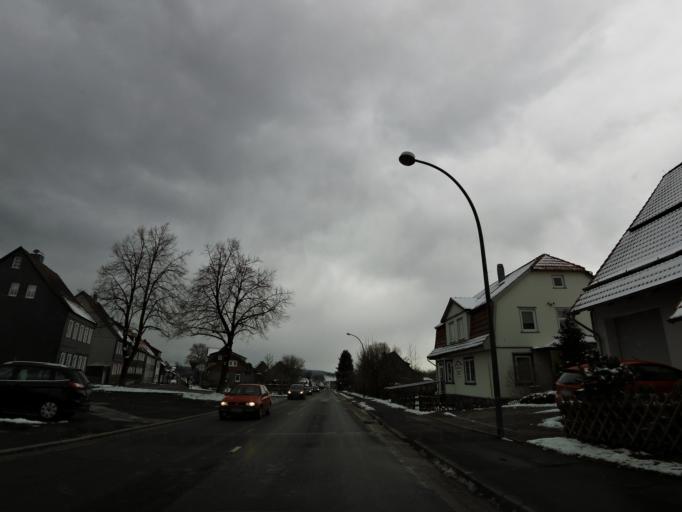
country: DE
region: Lower Saxony
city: Clausthal-Zellerfeld
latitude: 51.7969
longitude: 10.3376
